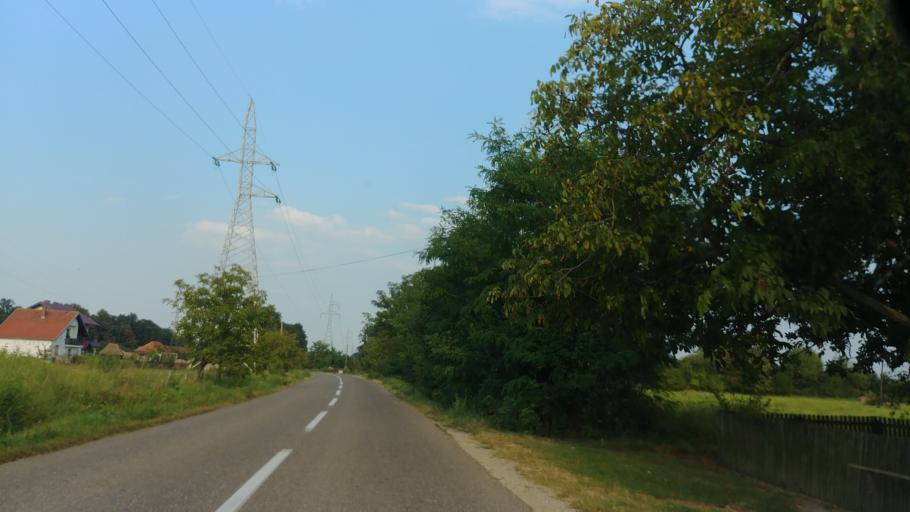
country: BA
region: Republika Srpska
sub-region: Opstina Ugljevik
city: Ugljevik
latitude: 44.7078
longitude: 19.0021
